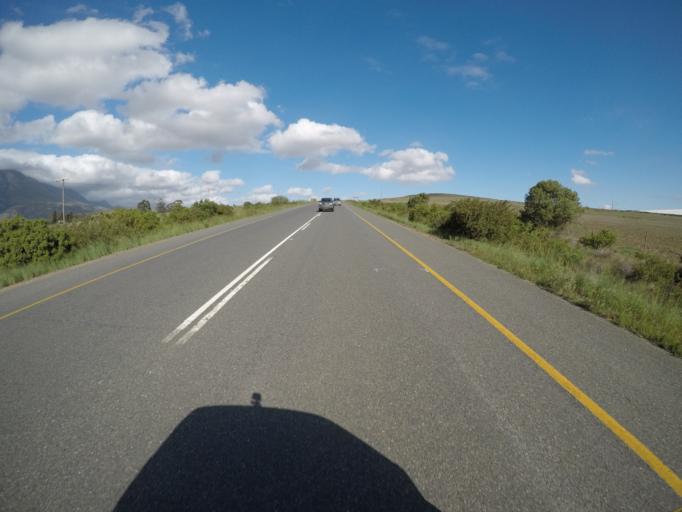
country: ZA
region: Western Cape
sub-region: Overberg District Municipality
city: Swellendam
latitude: -33.9661
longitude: 20.2471
